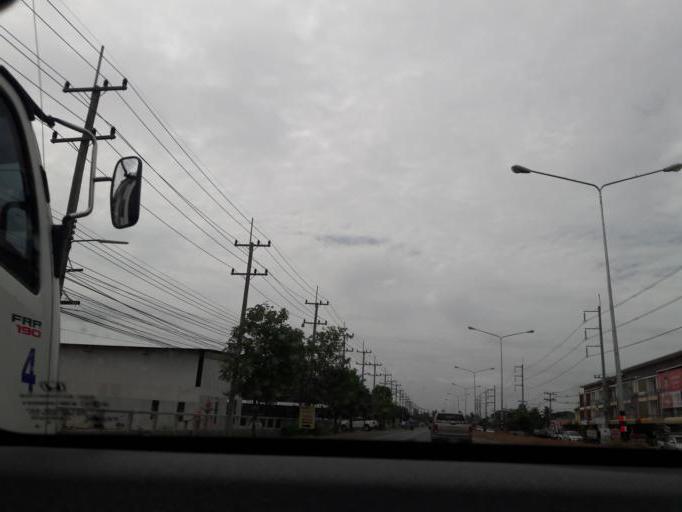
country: TH
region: Ratchaburi
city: Damnoen Saduak
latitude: 13.5767
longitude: 99.9694
